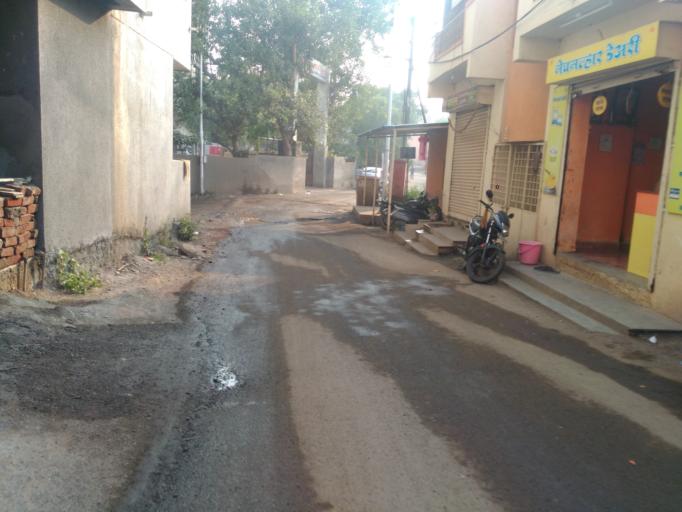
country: IN
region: Maharashtra
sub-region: Pune Division
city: Pune
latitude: 18.4355
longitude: 73.8909
